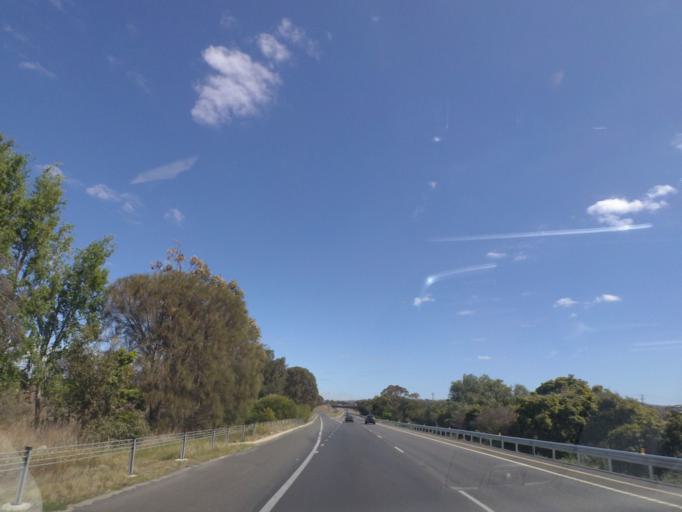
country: AU
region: Victoria
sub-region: Moorabool
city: Bacchus Marsh
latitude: -37.6644
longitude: 144.4446
